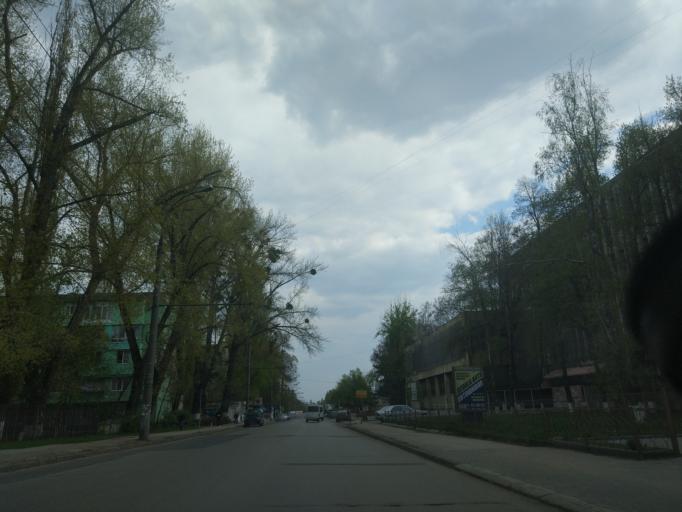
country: MD
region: Chisinau
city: Chisinau
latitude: 46.9850
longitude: 28.8756
